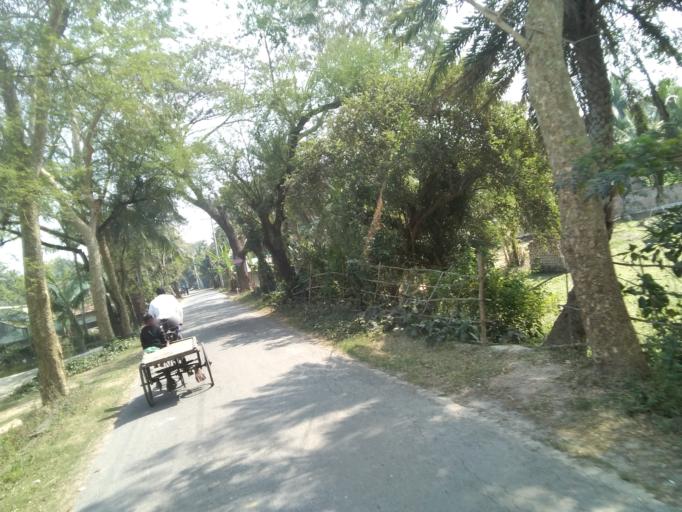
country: IN
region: West Bengal
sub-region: North 24 Parganas
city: Taki
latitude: 22.5923
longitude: 88.9915
